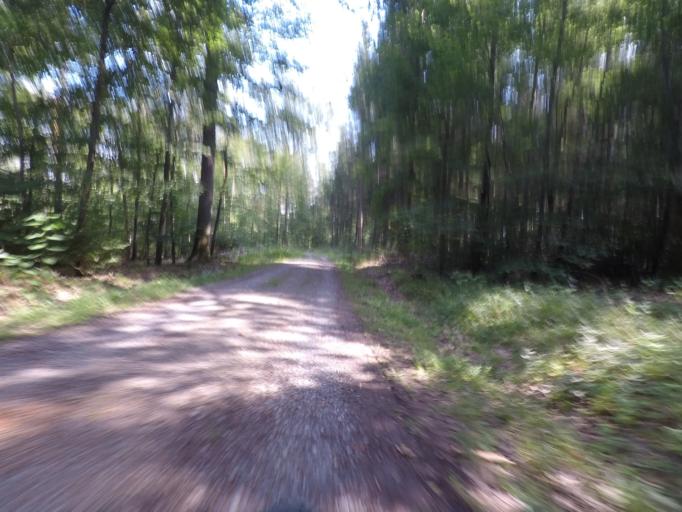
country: DE
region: Baden-Wuerttemberg
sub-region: Regierungsbezirk Stuttgart
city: Steinenbronn
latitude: 48.7016
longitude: 9.1020
